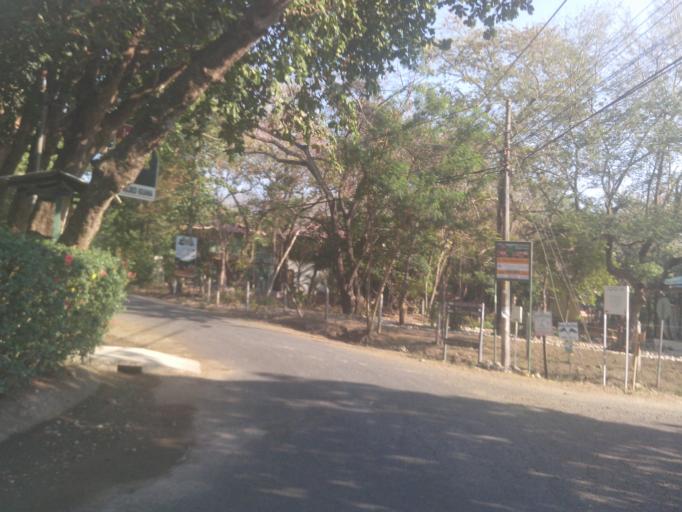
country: CR
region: Guanacaste
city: Samara
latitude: 9.9480
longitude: -85.6697
